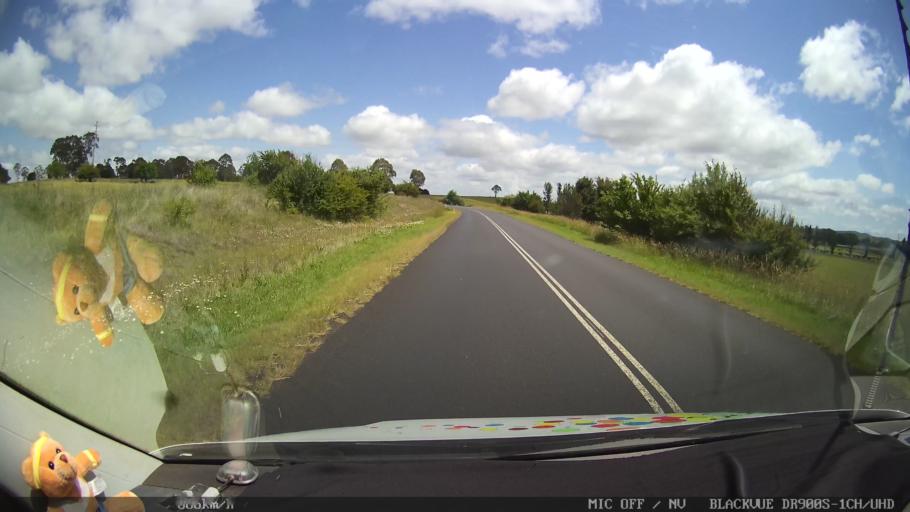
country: AU
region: New South Wales
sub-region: Glen Innes Severn
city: Glen Innes
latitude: -29.7012
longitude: 151.7188
